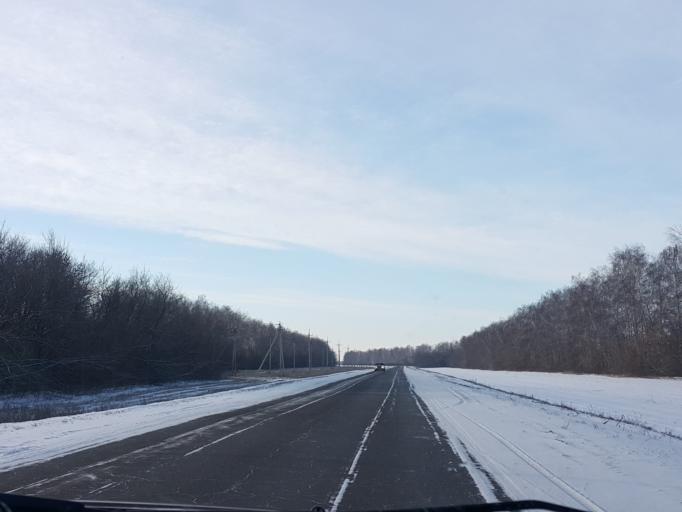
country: RU
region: Tambov
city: Znamenka
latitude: 52.4013
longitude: 41.3843
